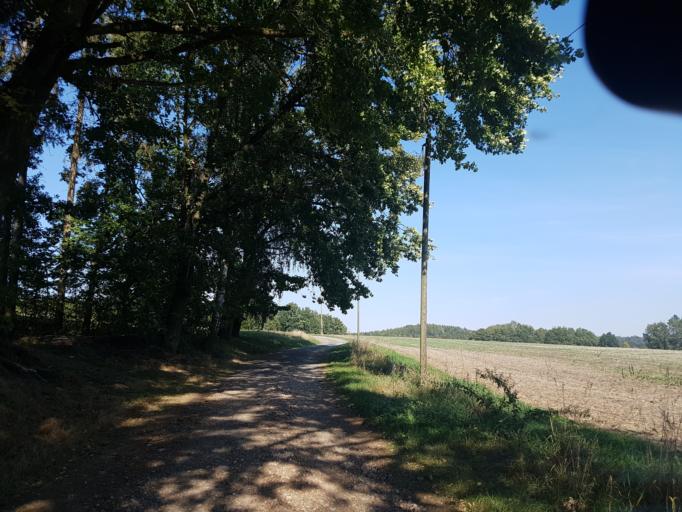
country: DE
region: Saxony
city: Kriebstein
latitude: 51.0448
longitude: 13.0071
